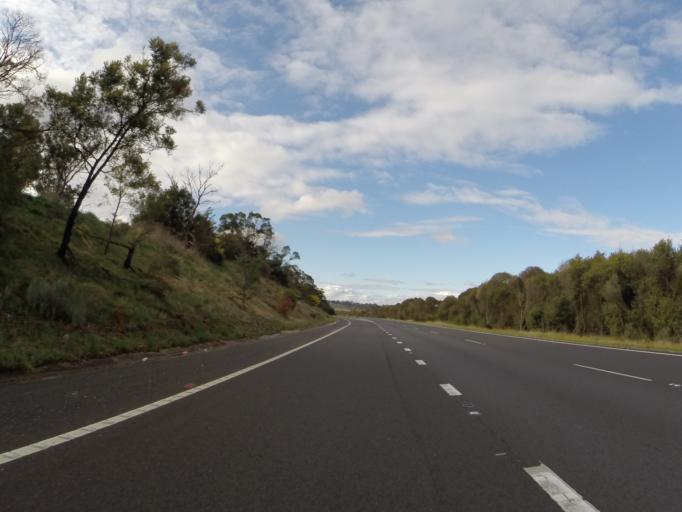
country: AU
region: New South Wales
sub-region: Wingecarribee
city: Bundanoon
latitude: -34.5913
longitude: 150.2459
